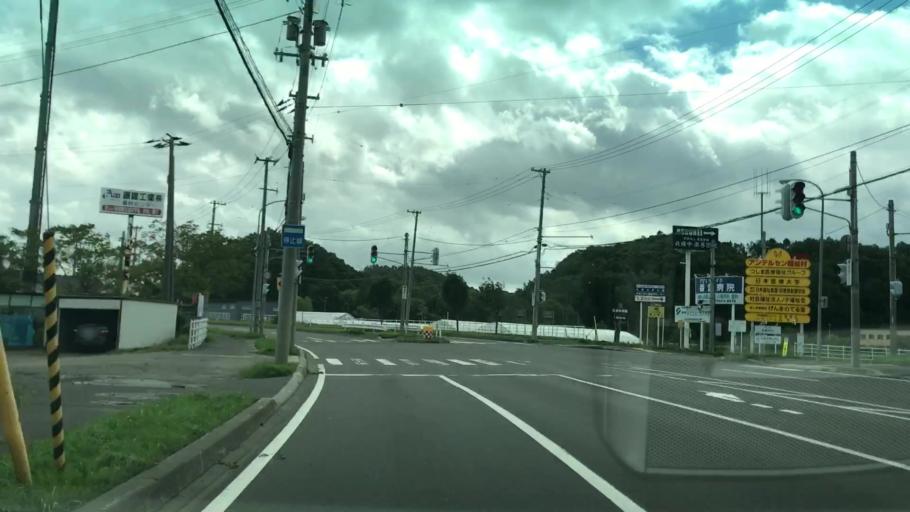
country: JP
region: Hokkaido
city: Sapporo
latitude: 42.9794
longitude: 141.4391
